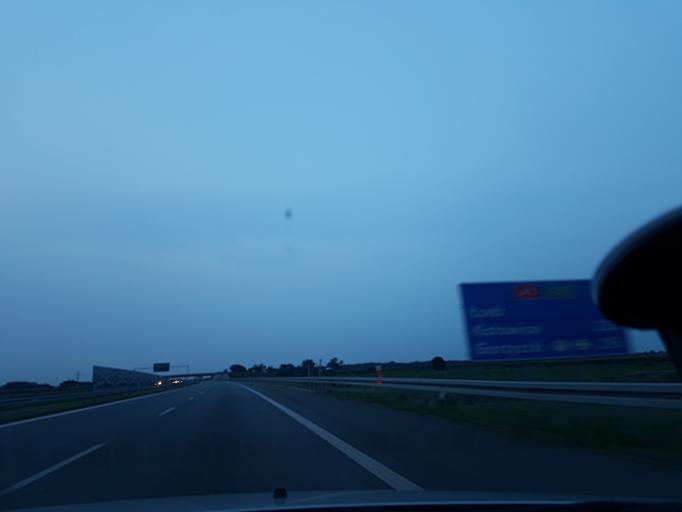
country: PL
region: Lodz Voivodeship
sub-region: Powiat leczycki
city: Piatek
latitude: 52.0526
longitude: 19.5359
